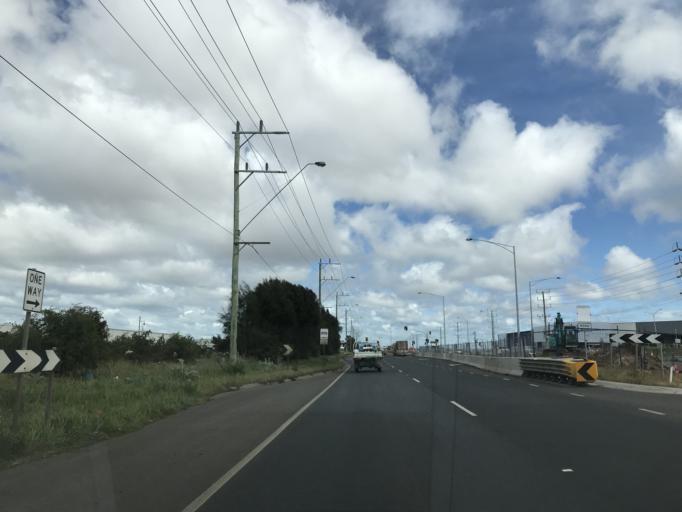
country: AU
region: Victoria
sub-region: Brimbank
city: Derrimut
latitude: -37.7978
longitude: 144.7526
